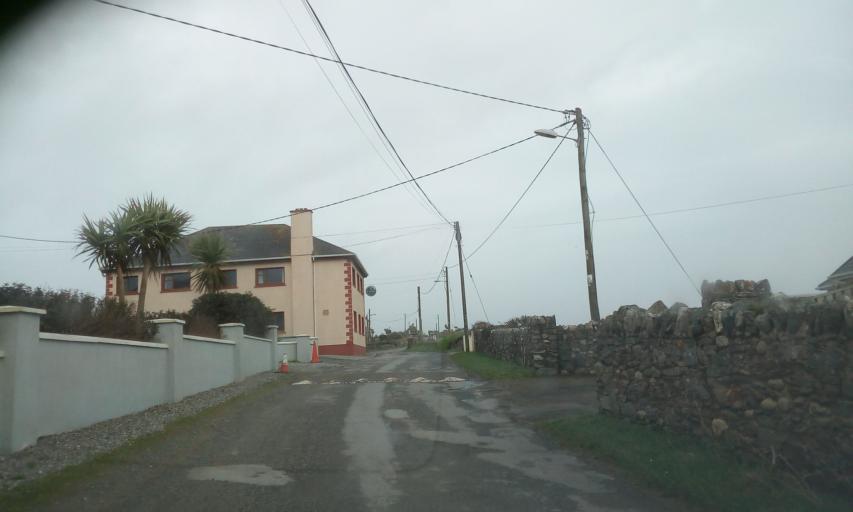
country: IE
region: Munster
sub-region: Waterford
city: Dunmore East
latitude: 52.2176
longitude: -6.7186
